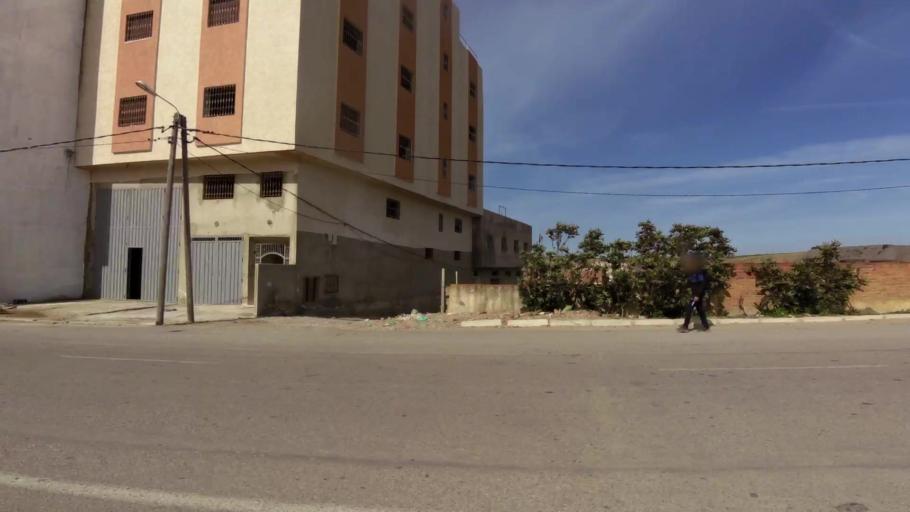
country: MA
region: Tanger-Tetouan
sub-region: Tanger-Assilah
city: Tangier
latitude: 35.7040
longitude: -5.8051
